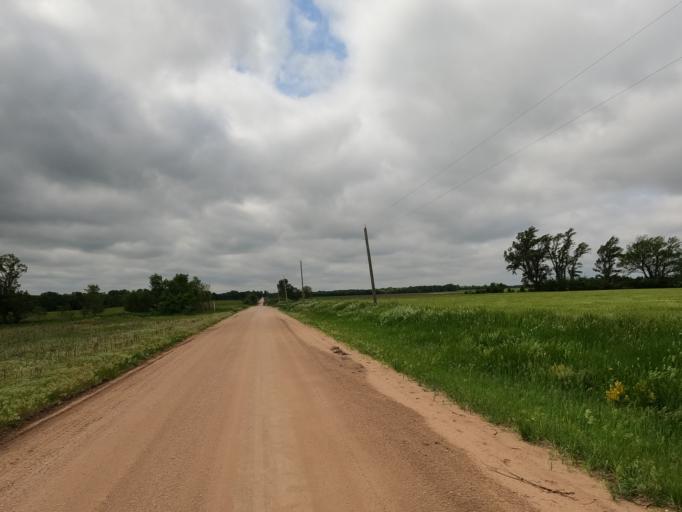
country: US
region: Kansas
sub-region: McPherson County
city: McPherson
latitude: 38.2975
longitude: -97.6119
